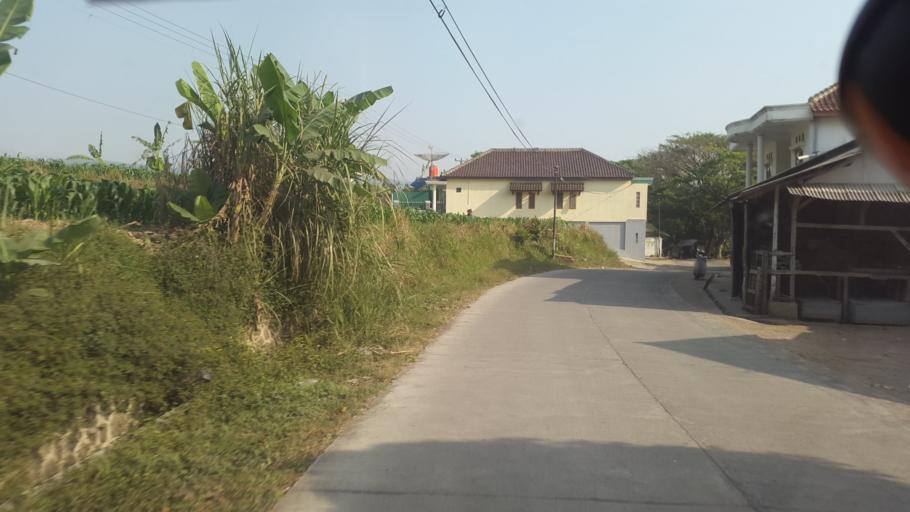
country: ID
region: West Java
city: Sukabumi
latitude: -6.9449
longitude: 106.9663
